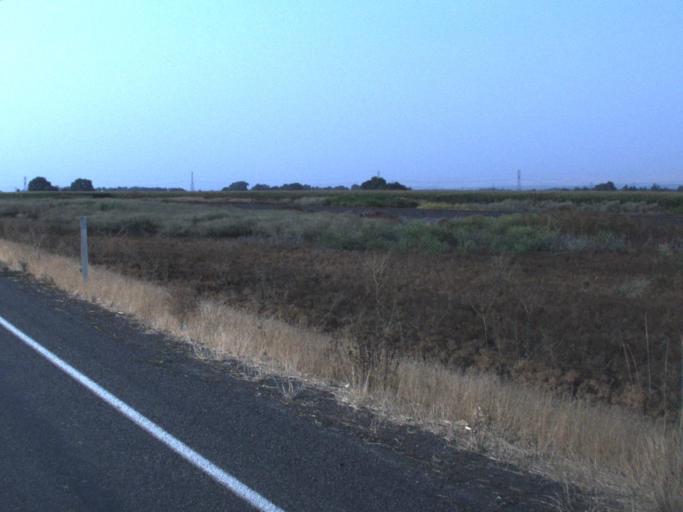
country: US
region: Washington
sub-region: Yakima County
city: Granger
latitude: 46.2940
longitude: -120.1855
